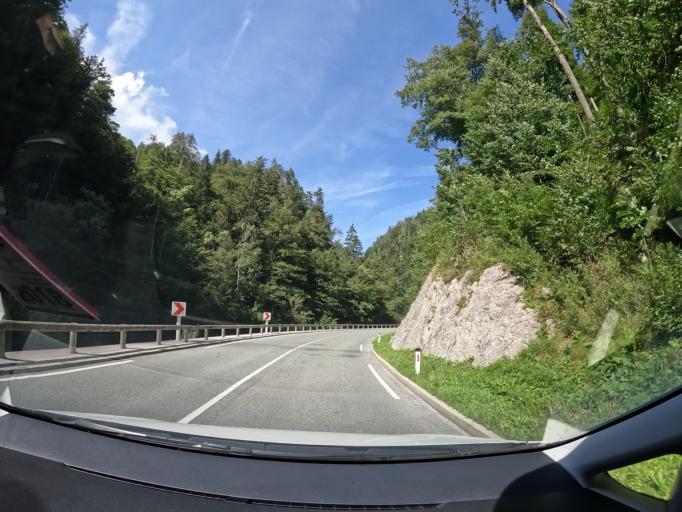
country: SI
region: Trzic
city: Trzic
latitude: 46.4031
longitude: 14.3237
